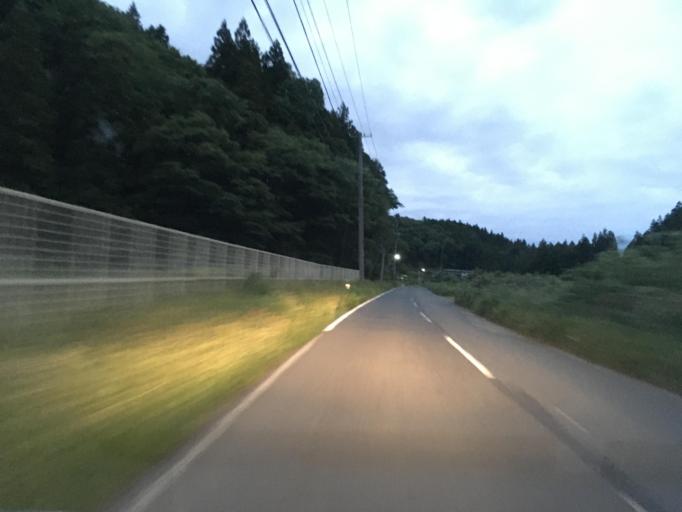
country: JP
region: Miyagi
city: Furukawa
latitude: 38.7659
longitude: 140.8785
